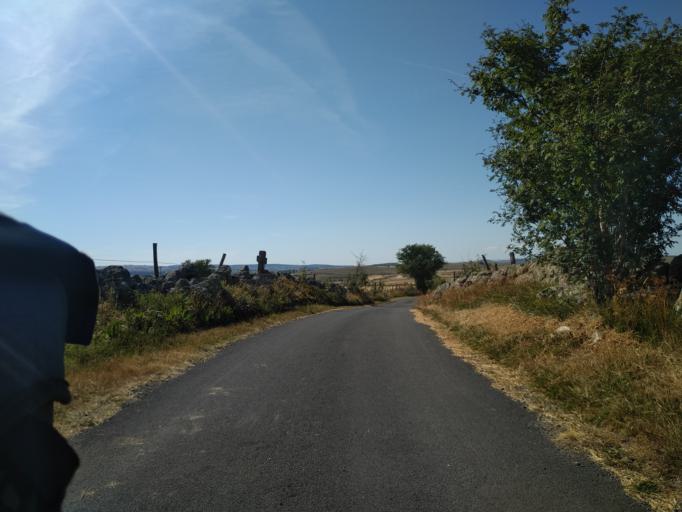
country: FR
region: Languedoc-Roussillon
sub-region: Departement de la Lozere
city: Aumont-Aubrac
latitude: 44.6708
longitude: 3.1016
